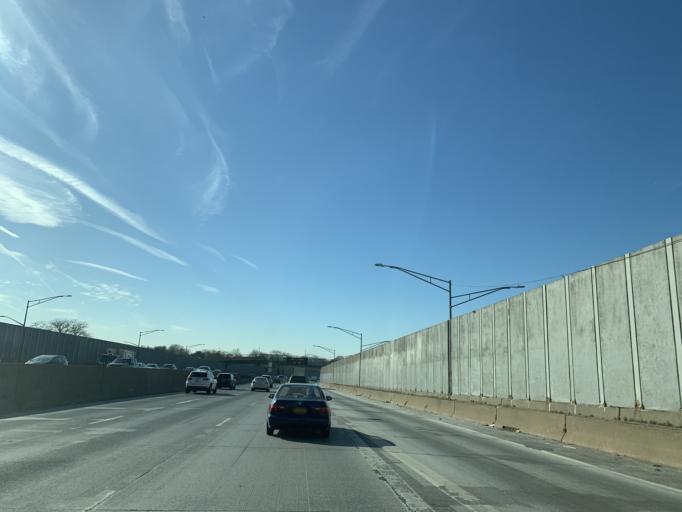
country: US
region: New York
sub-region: Kings County
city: East New York
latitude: 40.7278
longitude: -73.8886
